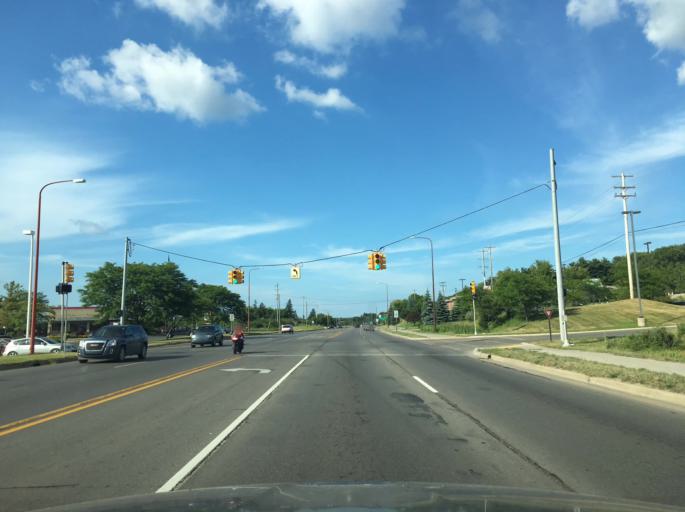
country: US
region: Michigan
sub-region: Grand Traverse County
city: Traverse City
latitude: 44.7432
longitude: -85.6413
